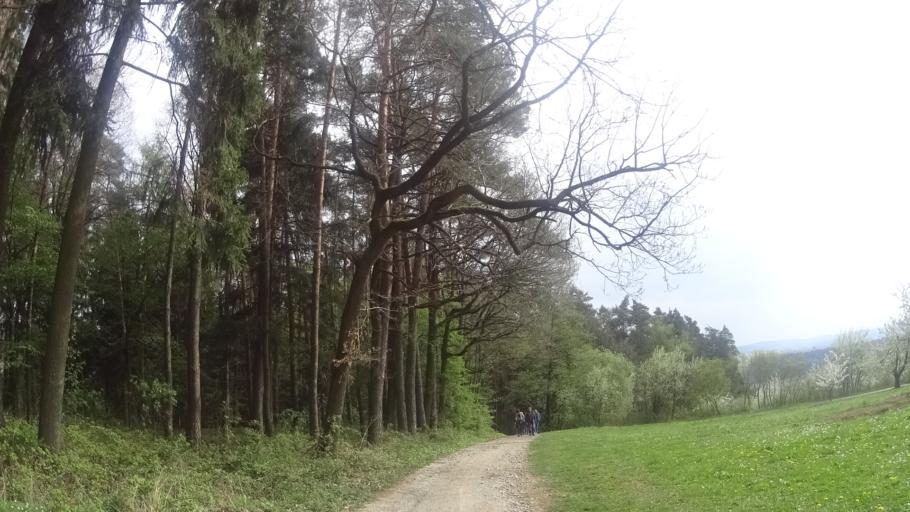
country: DE
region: Bavaria
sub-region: Upper Franconia
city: Igensdorf
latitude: 49.6243
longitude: 11.2115
